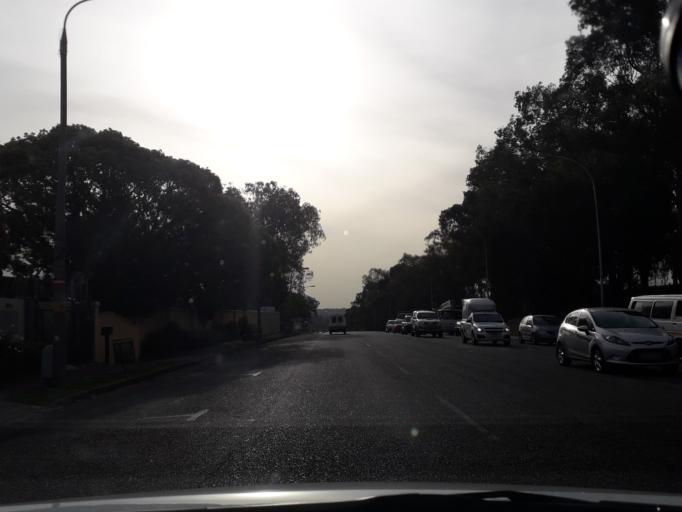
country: ZA
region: Gauteng
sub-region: City of Johannesburg Metropolitan Municipality
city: Modderfontein
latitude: -26.1499
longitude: 28.1460
